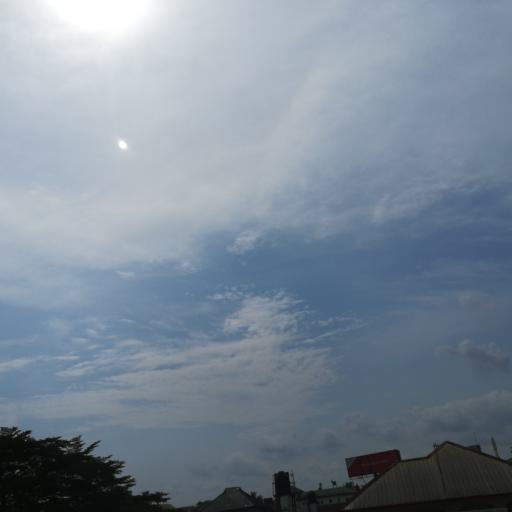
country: NG
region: Rivers
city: Port Harcourt
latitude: 4.8599
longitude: 7.0215
